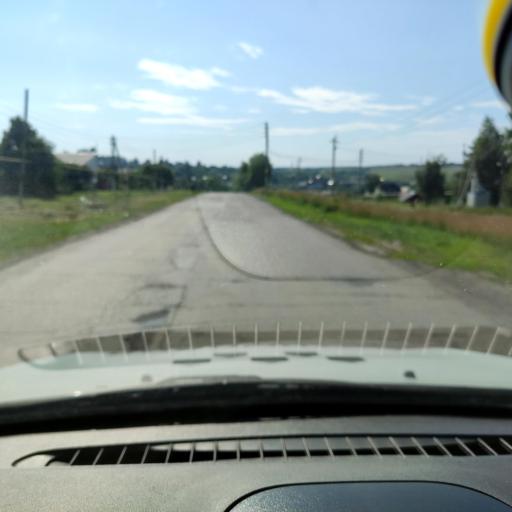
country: RU
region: Samara
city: Tol'yatti
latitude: 53.3549
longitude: 49.3152
